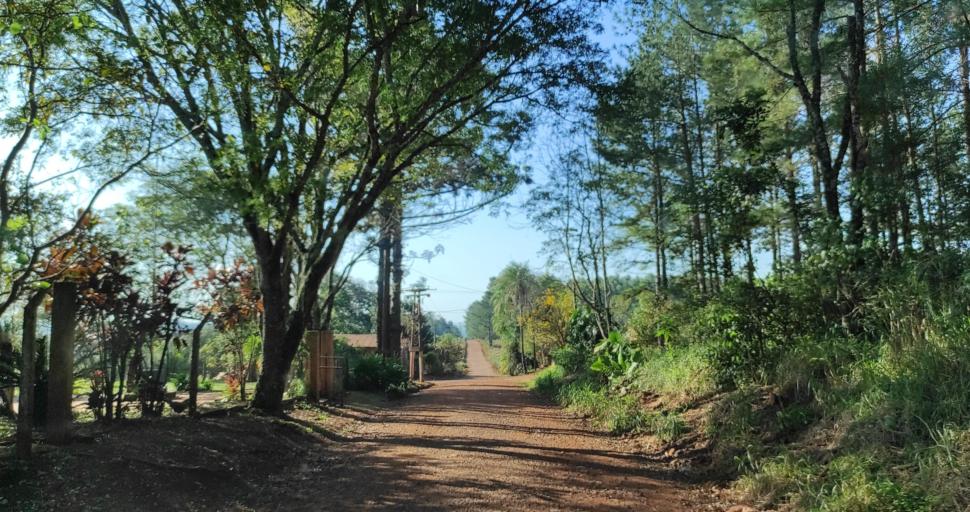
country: AR
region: Misiones
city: Capiovi
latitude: -26.8740
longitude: -55.1078
